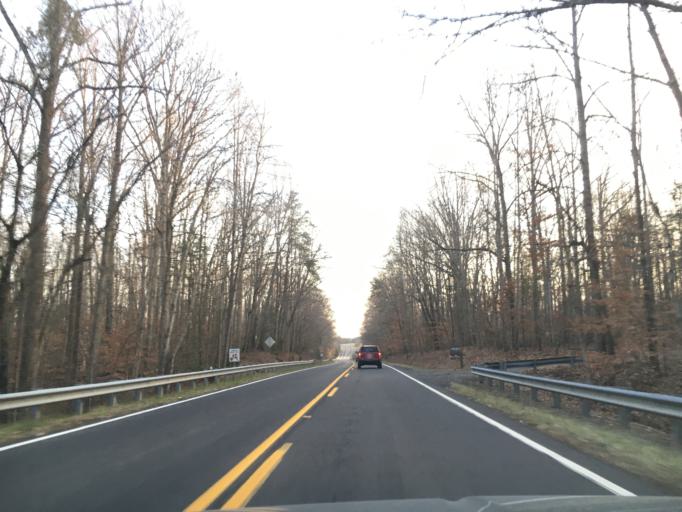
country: US
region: Virginia
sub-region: Louisa County
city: Louisa
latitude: 38.1473
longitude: -77.9262
